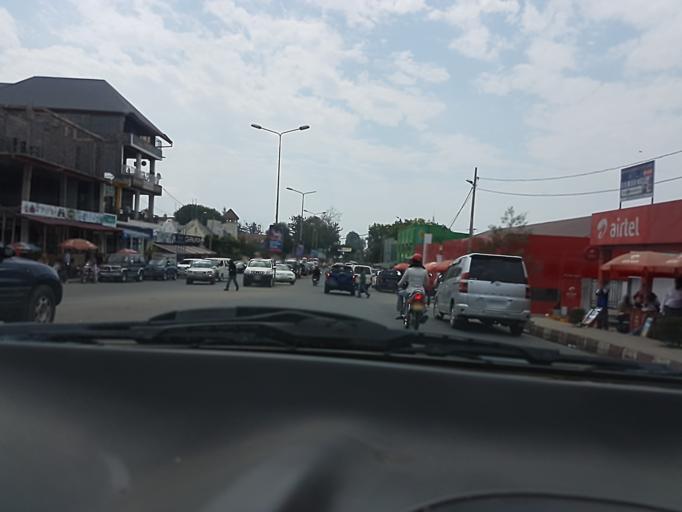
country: CD
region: Nord Kivu
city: Goma
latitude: -1.6864
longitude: 29.2362
